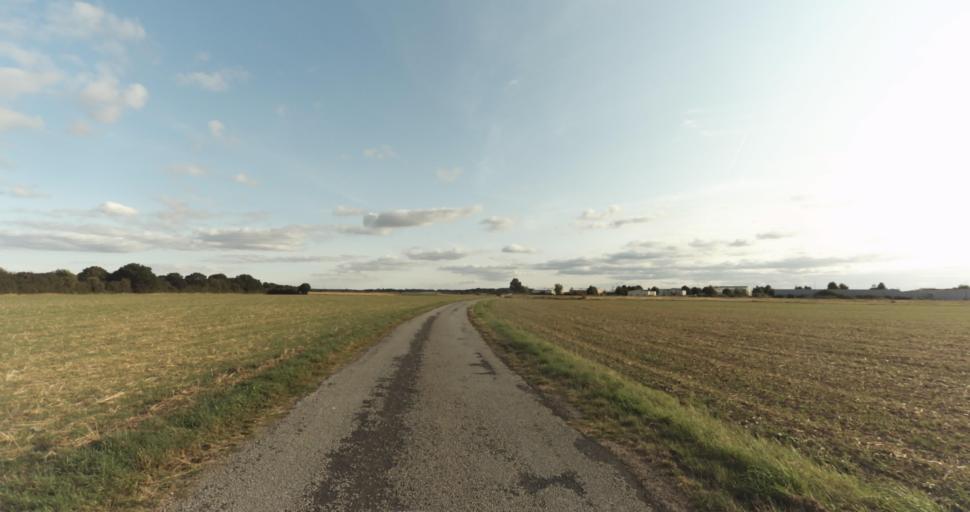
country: FR
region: Haute-Normandie
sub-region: Departement de l'Eure
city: Marcilly-sur-Eure
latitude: 48.8969
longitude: 1.2754
